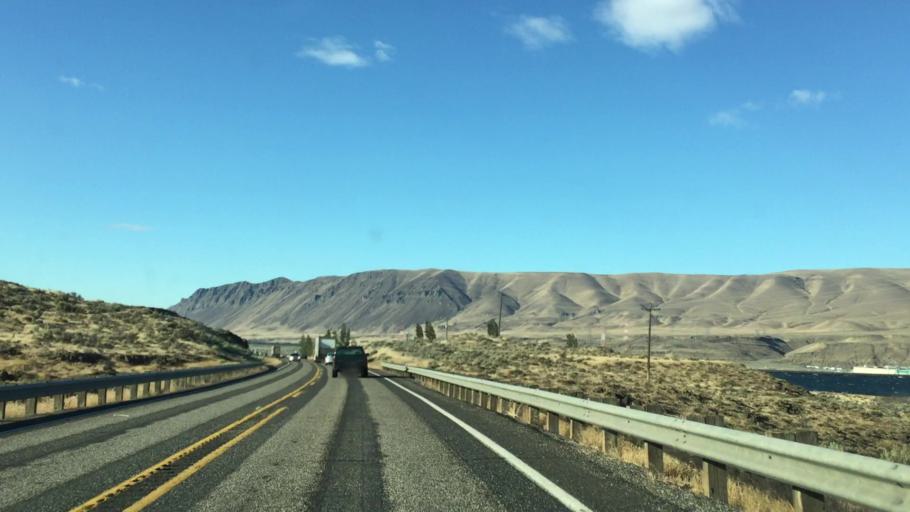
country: US
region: Washington
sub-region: Grant County
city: Mattawa
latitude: 46.8887
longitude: -119.9551
